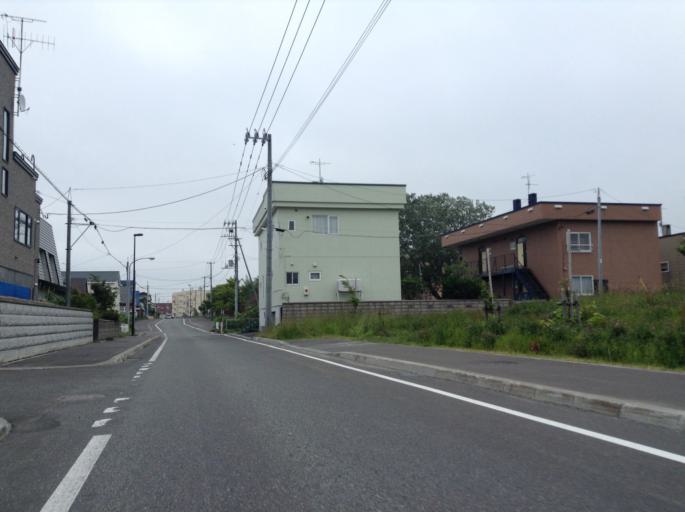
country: JP
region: Hokkaido
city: Wakkanai
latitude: 45.3962
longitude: 141.6888
